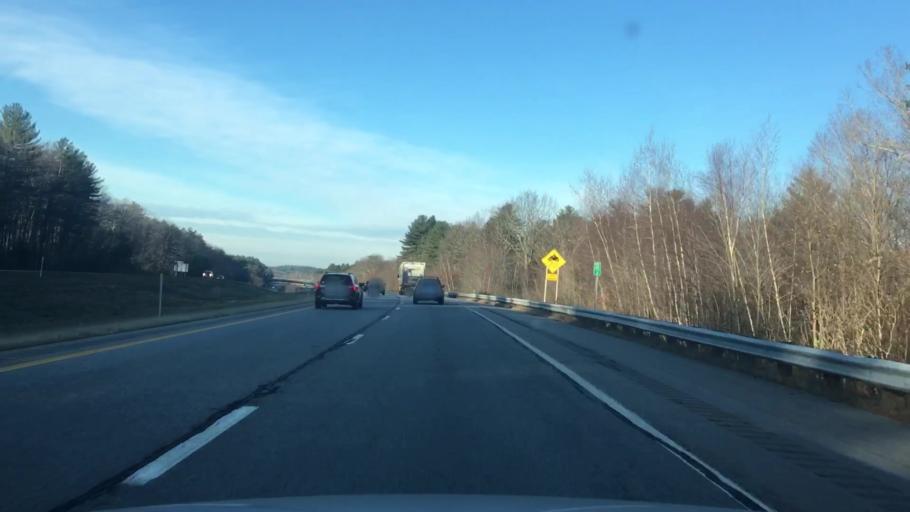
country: US
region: New Hampshire
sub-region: Rockingham County
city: Fremont
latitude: 43.0317
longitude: -71.1344
